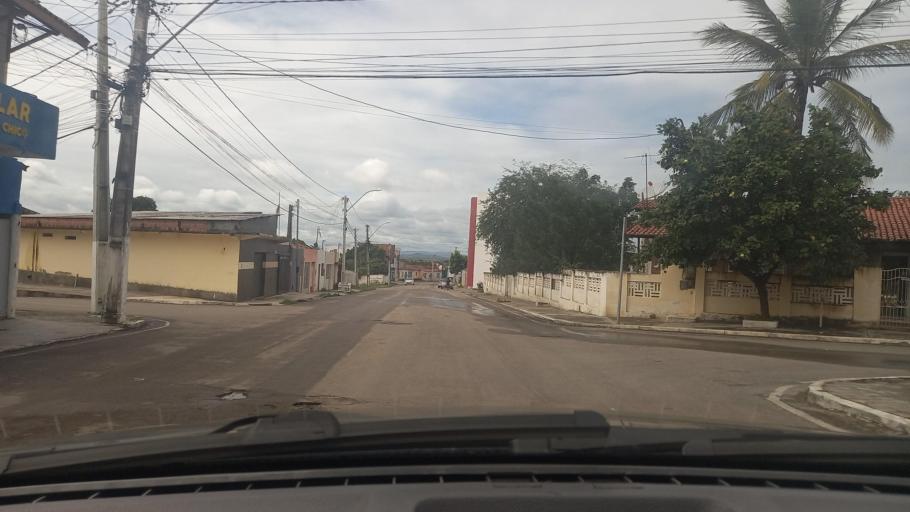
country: BR
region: Bahia
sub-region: Paulo Afonso
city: Paulo Afonso
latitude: -9.4452
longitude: -38.2205
